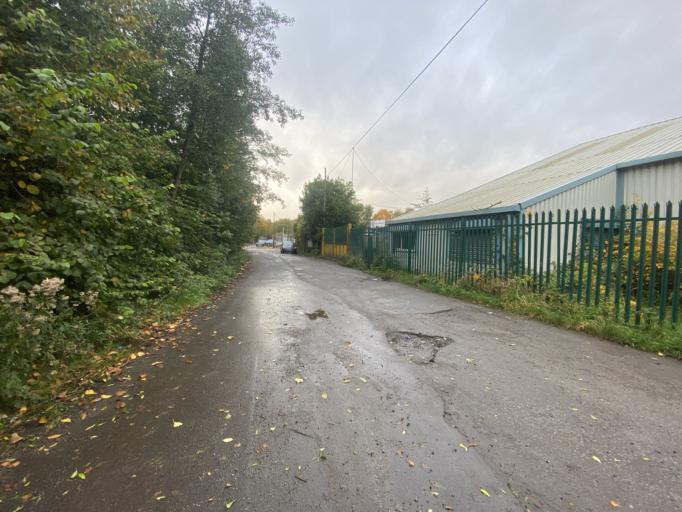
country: GB
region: England
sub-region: St. Helens
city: Haydock
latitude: 53.4418
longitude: -2.6993
